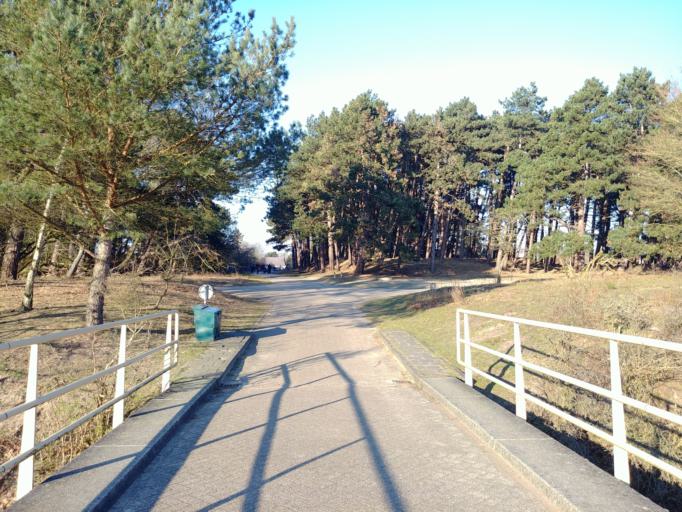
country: NL
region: North Holland
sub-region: Gemeente Zandvoort
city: Zandvoort
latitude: 52.3626
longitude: 4.5533
